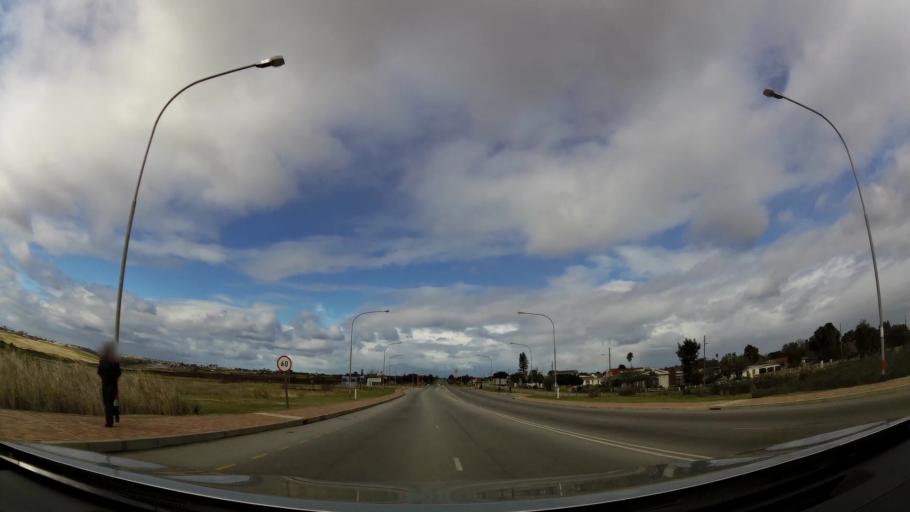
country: ZA
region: Western Cape
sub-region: Eden District Municipality
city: George
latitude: -34.0008
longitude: 22.4466
